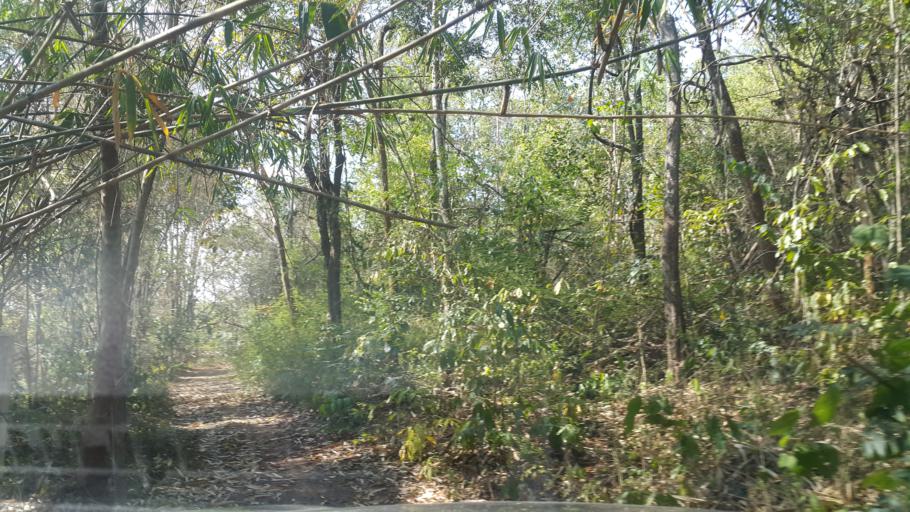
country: TH
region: Sukhothai
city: Thung Saliam
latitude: 17.3556
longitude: 99.5779
